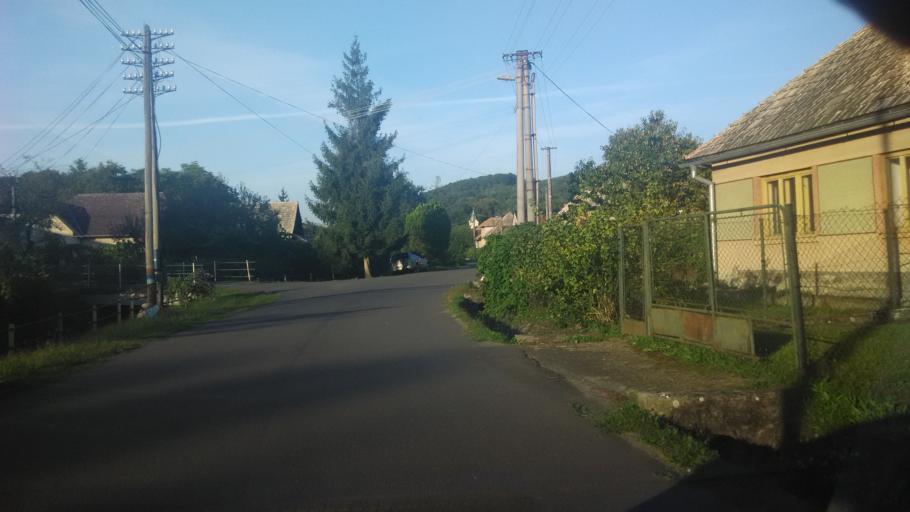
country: SK
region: Banskobystricky
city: Dudince
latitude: 48.2249
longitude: 18.8618
